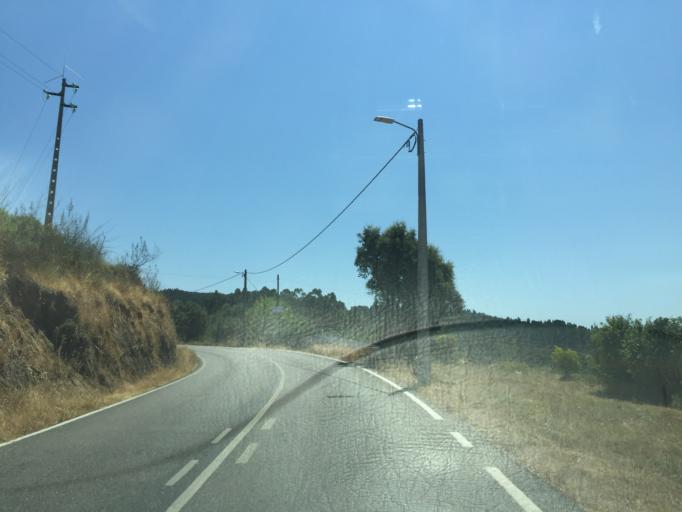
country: PT
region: Santarem
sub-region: Tomar
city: Tomar
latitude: 39.5909
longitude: -8.3553
